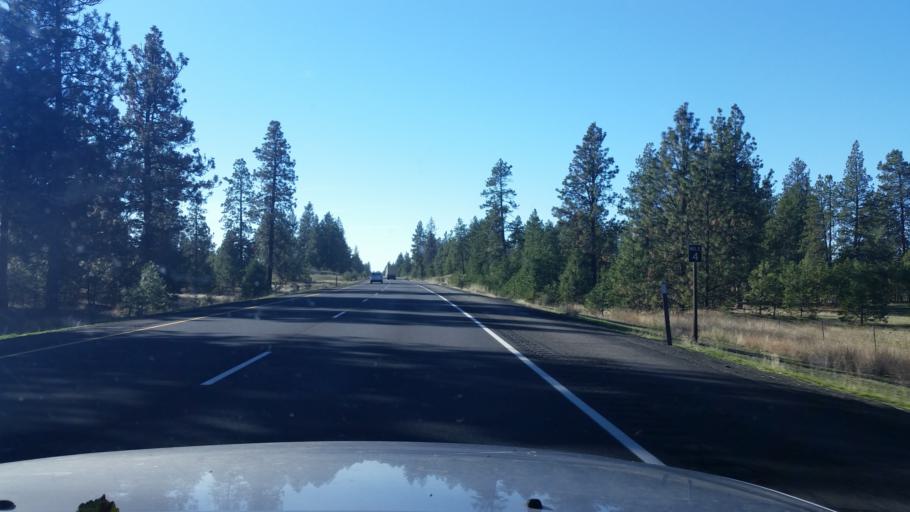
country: US
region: Washington
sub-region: Spokane County
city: Medical Lake
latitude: 47.4240
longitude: -117.8064
